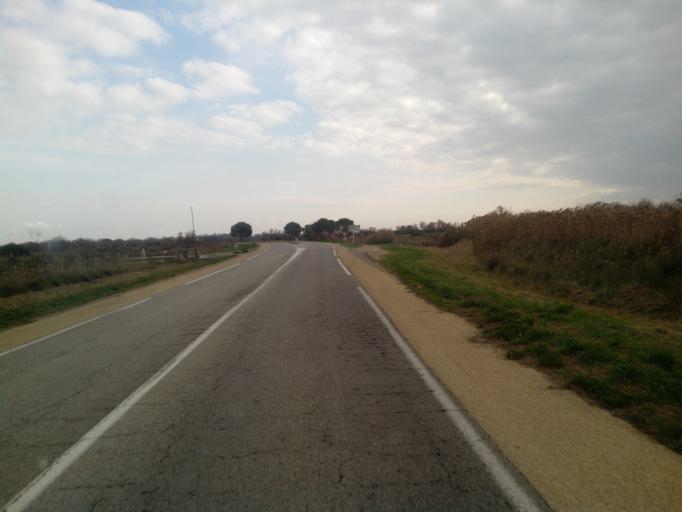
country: FR
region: Provence-Alpes-Cote d'Azur
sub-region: Departement des Bouches-du-Rhone
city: Saintes-Maries-de-la-Mer
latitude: 43.5481
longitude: 4.3987
